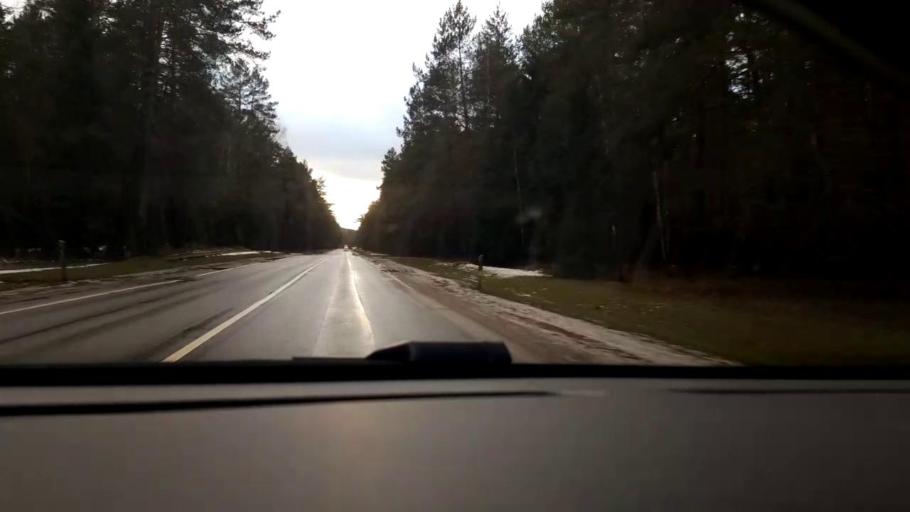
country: LT
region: Vilnius County
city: Rasos
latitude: 54.7688
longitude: 25.3794
